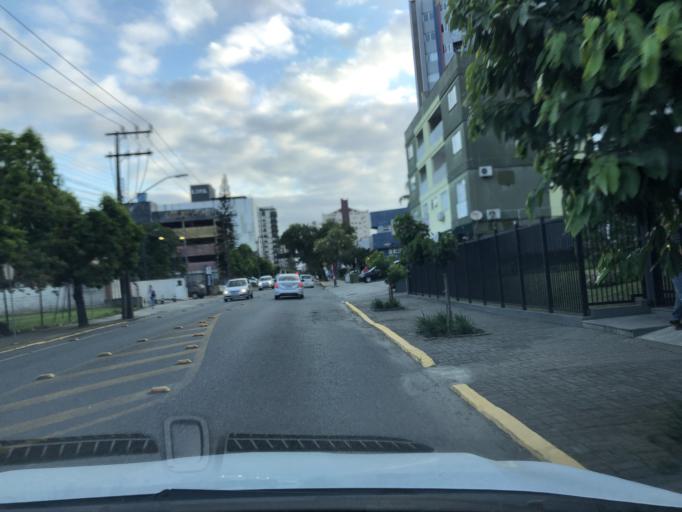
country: BR
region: Santa Catarina
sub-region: Joinville
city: Joinville
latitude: -26.2907
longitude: -48.8455
